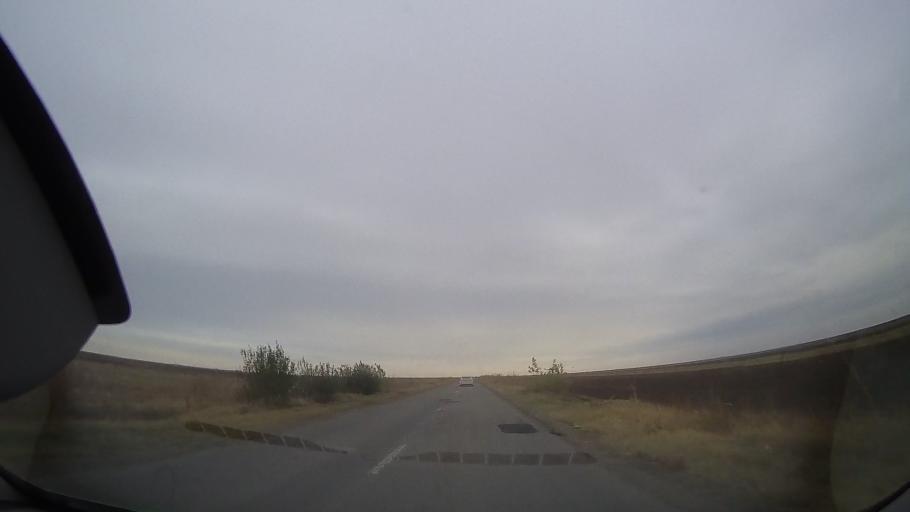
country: RO
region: Ialomita
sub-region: Oras Amara
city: Amara
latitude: 44.6622
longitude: 27.3007
